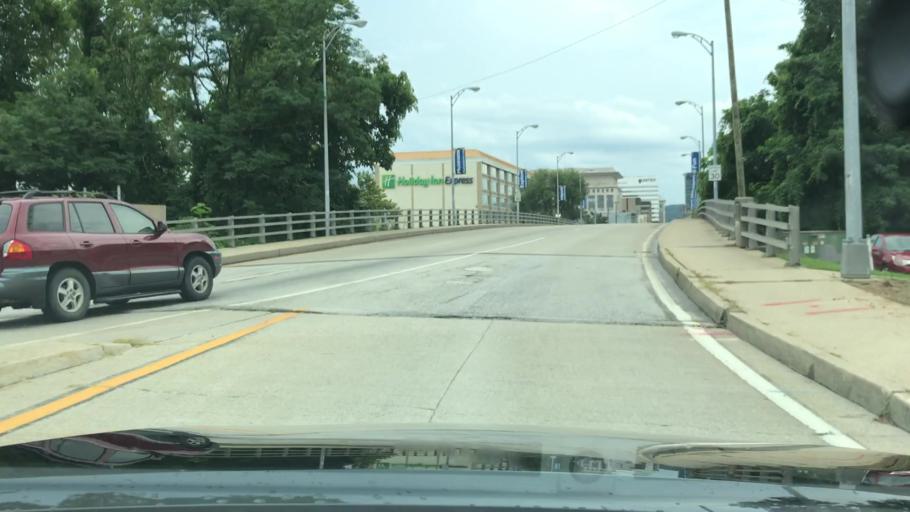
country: US
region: West Virginia
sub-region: Kanawha County
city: Charleston
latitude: 38.3562
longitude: -81.6444
